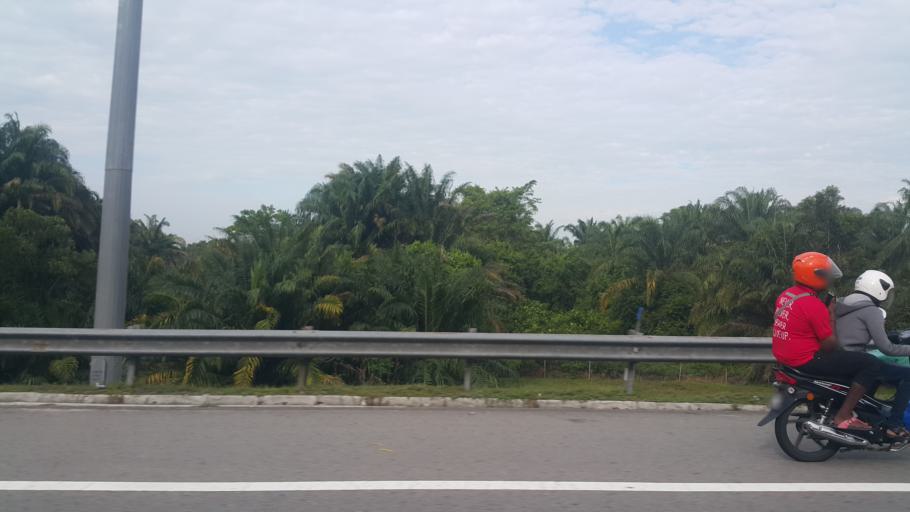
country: MY
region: Johor
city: Pekan Nenas
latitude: 1.3850
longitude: 103.5926
